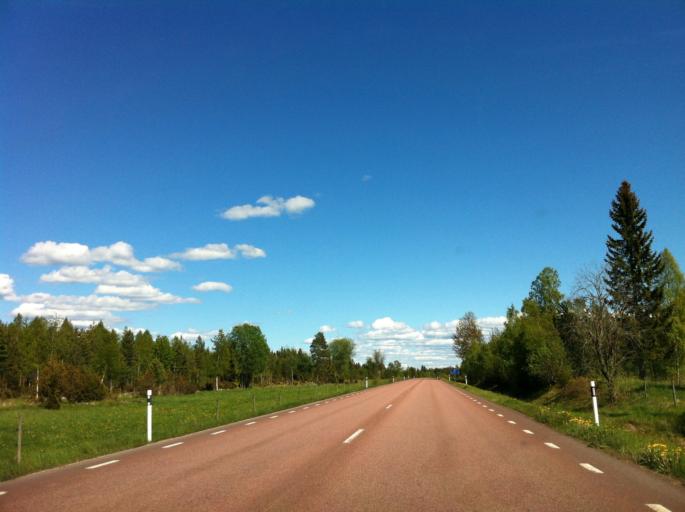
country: SE
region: Dalarna
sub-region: Leksand Municipality
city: Siljansnas
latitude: 60.9242
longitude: 14.8170
